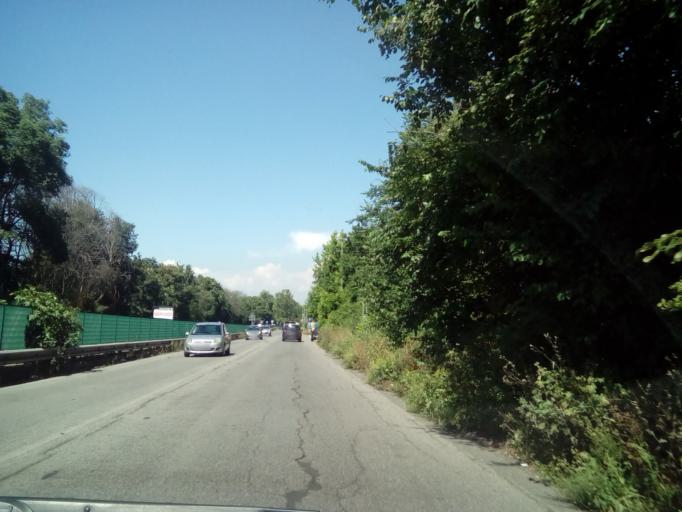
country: VA
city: Vatican City
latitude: 41.8380
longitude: 12.4606
